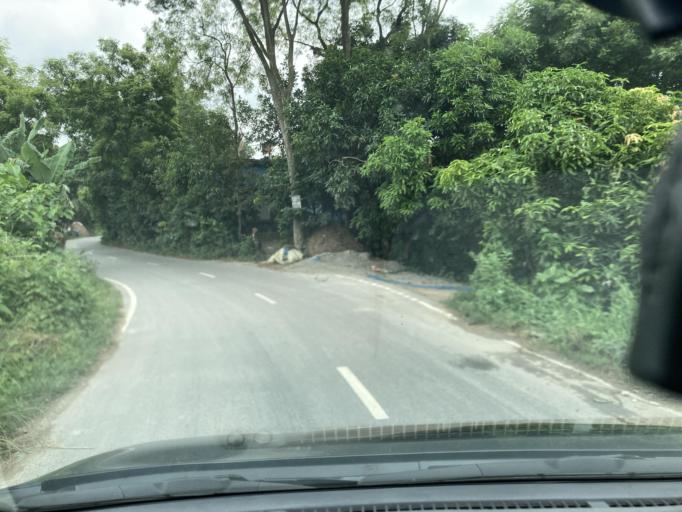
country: BD
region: Dhaka
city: Azimpur
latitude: 23.7812
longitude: 90.2119
